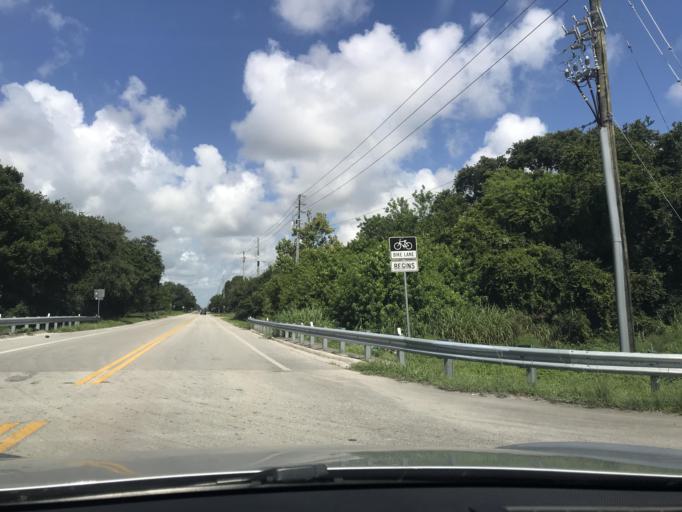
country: US
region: Florida
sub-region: Indian River County
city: Gifford
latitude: 27.6824
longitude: -80.4177
